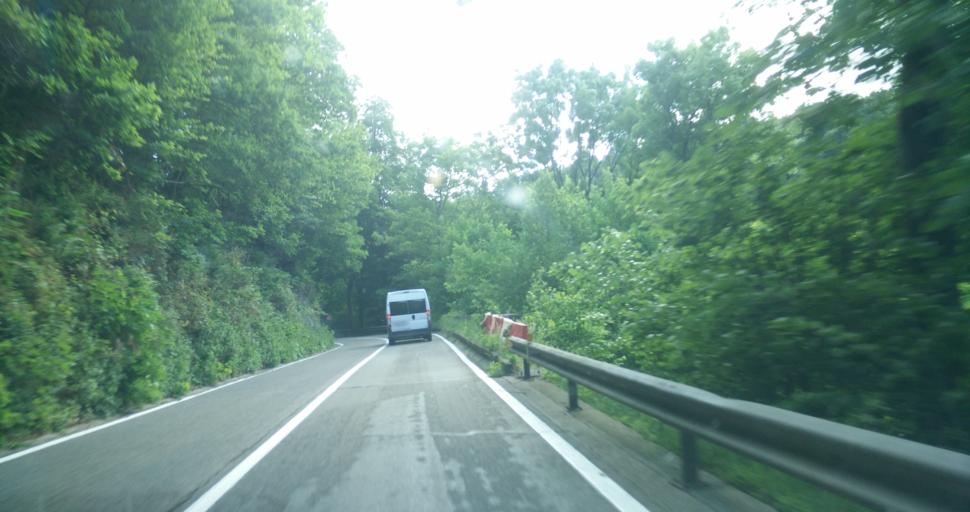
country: BE
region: Wallonia
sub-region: Province du Luxembourg
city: La Roche-en-Ardenne
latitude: 50.1764
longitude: 5.6081
